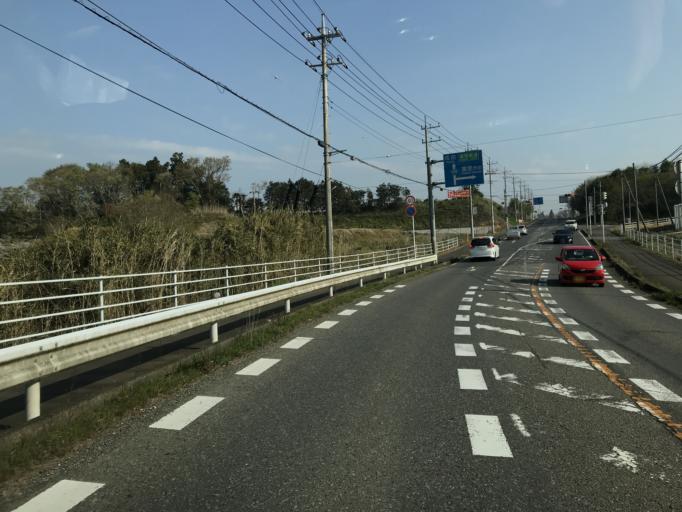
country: JP
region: Chiba
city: Shisui
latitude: 35.7303
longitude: 140.3151
